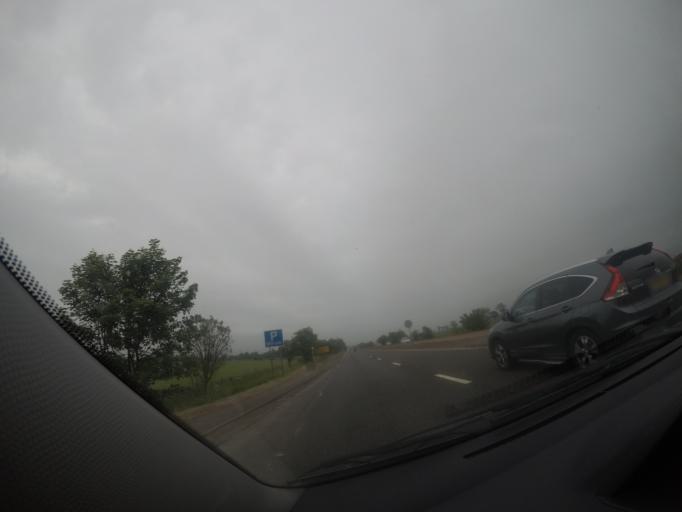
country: GB
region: Scotland
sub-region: Perth and Kinross
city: Errol
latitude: 56.4317
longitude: -3.2037
